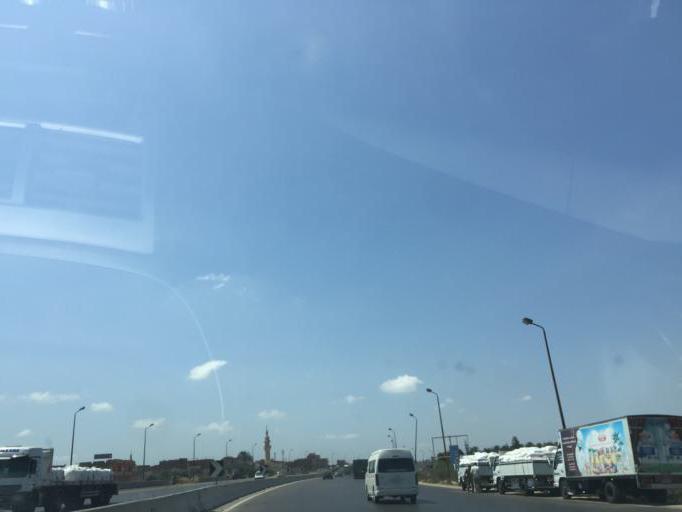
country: EG
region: Alexandria
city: Alexandria
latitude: 30.9773
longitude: 29.8184
